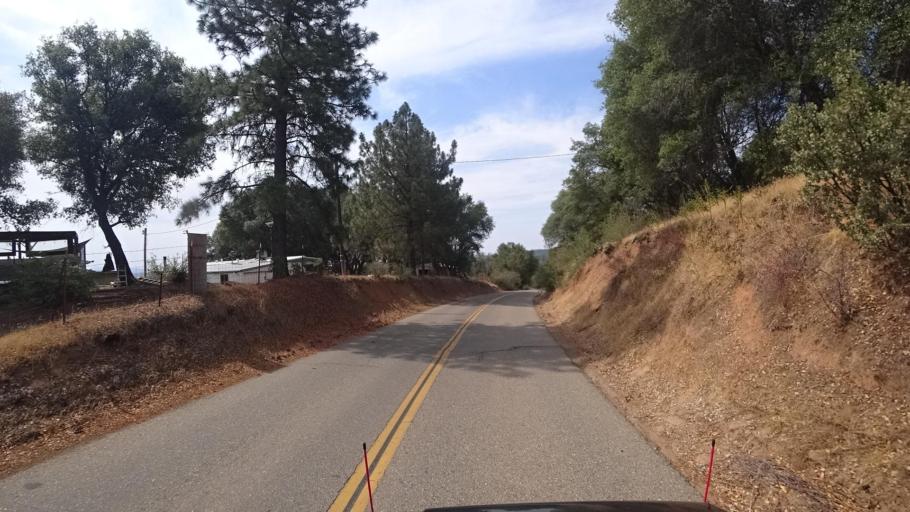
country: US
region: California
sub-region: Mariposa County
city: Midpines
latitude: 37.5007
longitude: -119.9070
